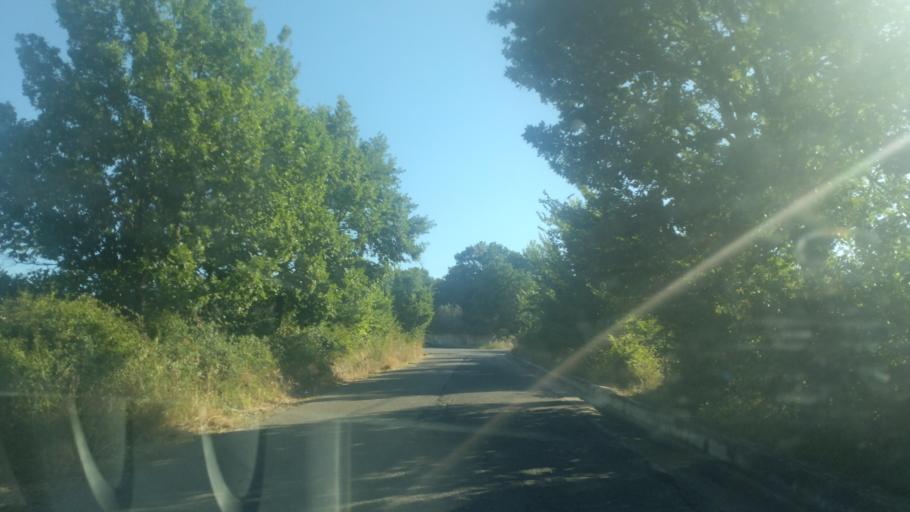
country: IT
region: Calabria
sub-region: Provincia di Catanzaro
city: Squillace
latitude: 38.7739
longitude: 16.5067
